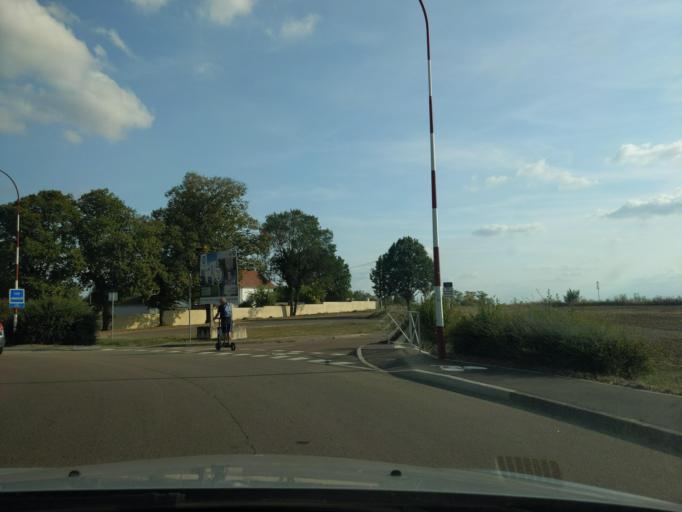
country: FR
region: Bourgogne
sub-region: Departement de la Cote-d'Or
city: Sennecey-les-Dijon
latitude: 47.2886
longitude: 5.0974
